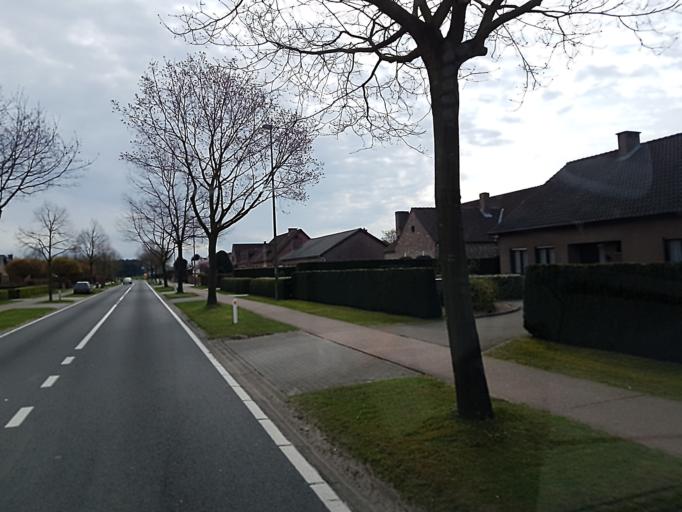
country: BE
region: Flanders
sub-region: Provincie Antwerpen
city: Westerlo
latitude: 51.0435
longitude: 4.9322
